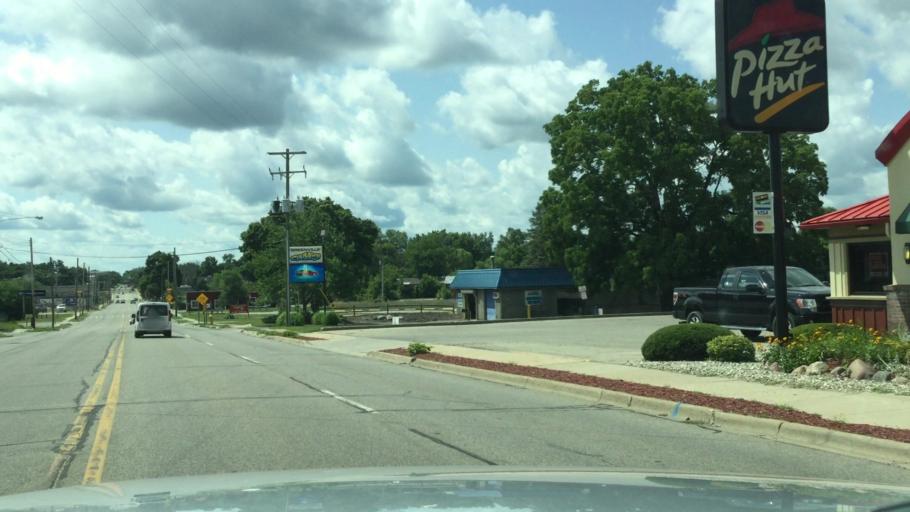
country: US
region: Michigan
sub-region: Montcalm County
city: Greenville
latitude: 43.1892
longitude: -85.2531
